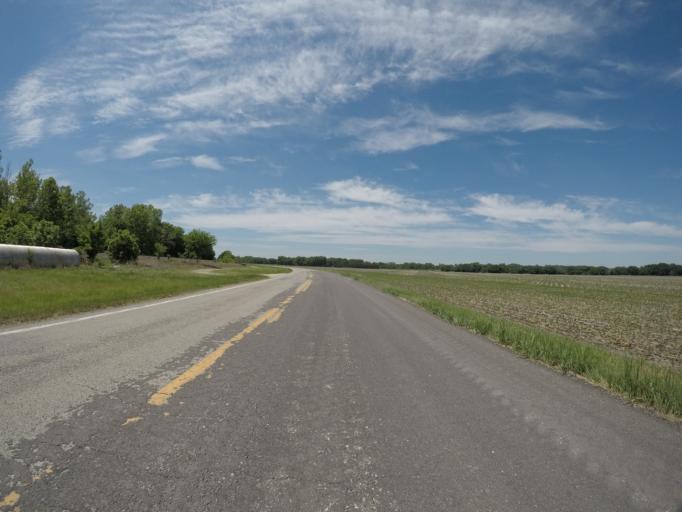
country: US
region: Kansas
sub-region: Wabaunsee County
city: Alma
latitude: 39.0414
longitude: -96.2635
